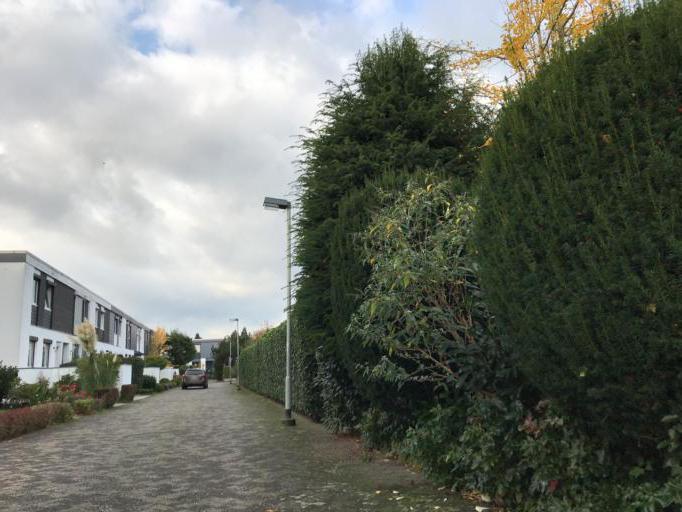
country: DE
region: Lower Saxony
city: Klein Schwulper
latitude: 52.2878
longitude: 10.4569
